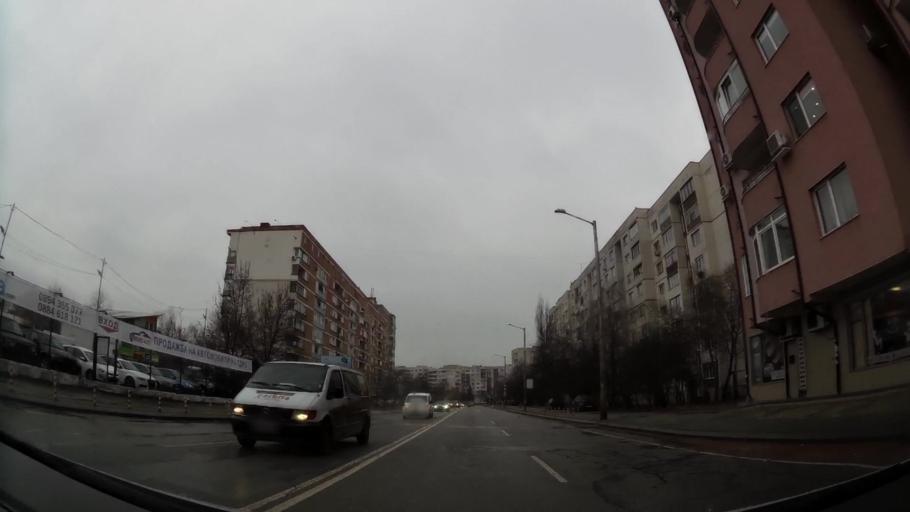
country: BG
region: Sofia-Capital
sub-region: Stolichna Obshtina
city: Sofia
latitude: 42.6381
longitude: 23.3750
